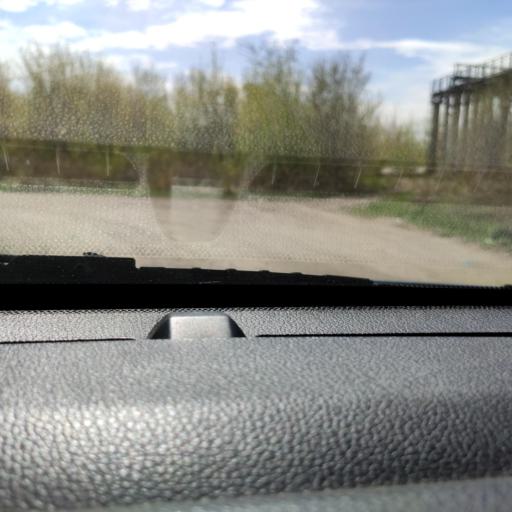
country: RU
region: Samara
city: Podstepki
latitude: 53.5764
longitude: 49.2278
